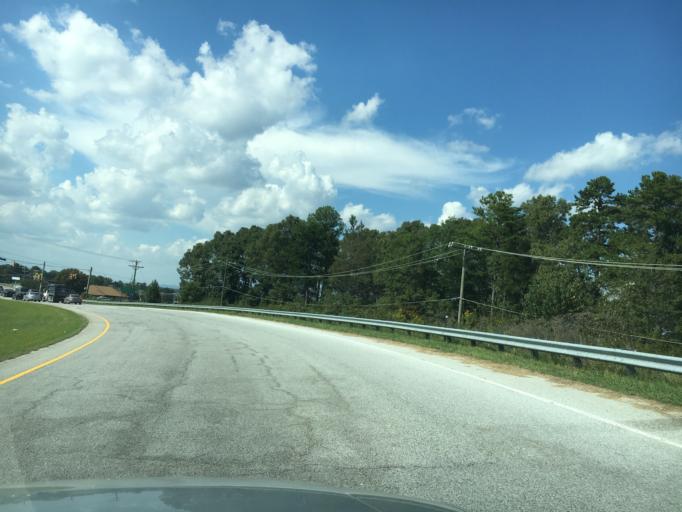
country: US
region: South Carolina
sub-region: Greenville County
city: Simpsonville
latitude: 34.7198
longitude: -82.2534
